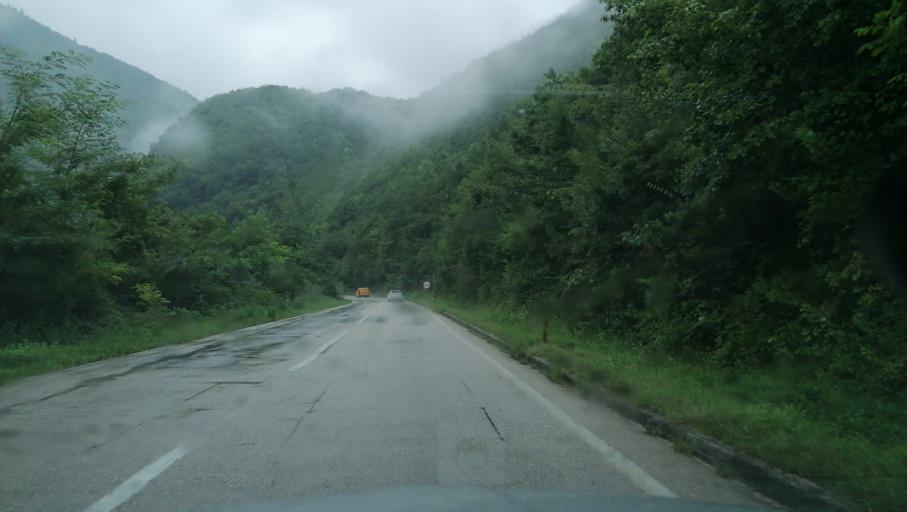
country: BA
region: Republika Srpska
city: Cajnice
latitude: 43.6841
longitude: 19.1510
